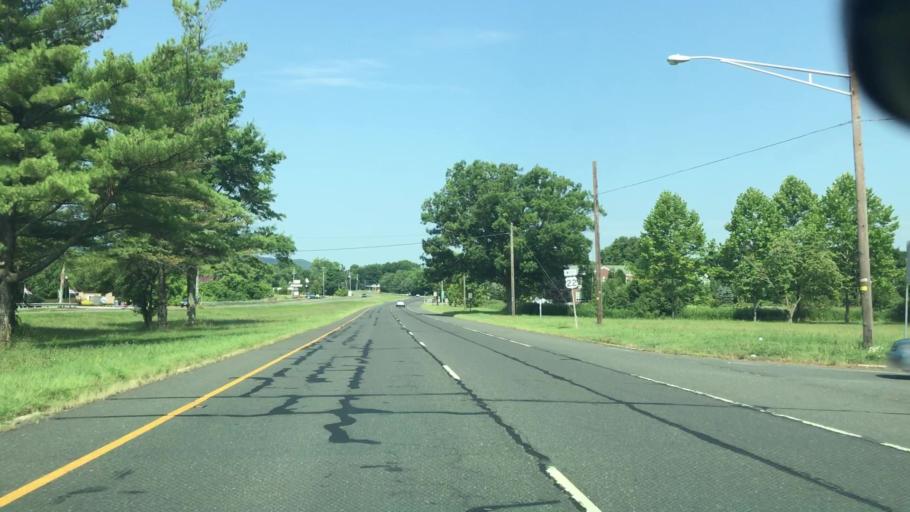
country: US
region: New Jersey
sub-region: Hunterdon County
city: Whitehouse Station
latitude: 40.6170
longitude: -74.7416
